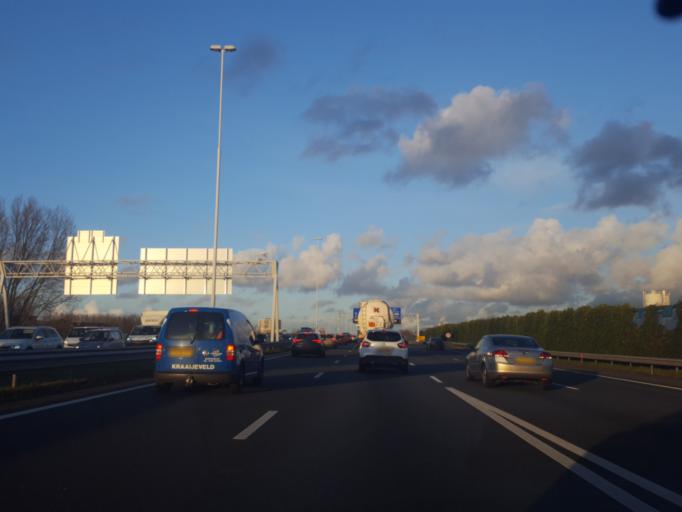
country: NL
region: South Holland
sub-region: Gemeente Rijswijk
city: Rijswijk
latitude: 52.0164
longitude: 4.3154
